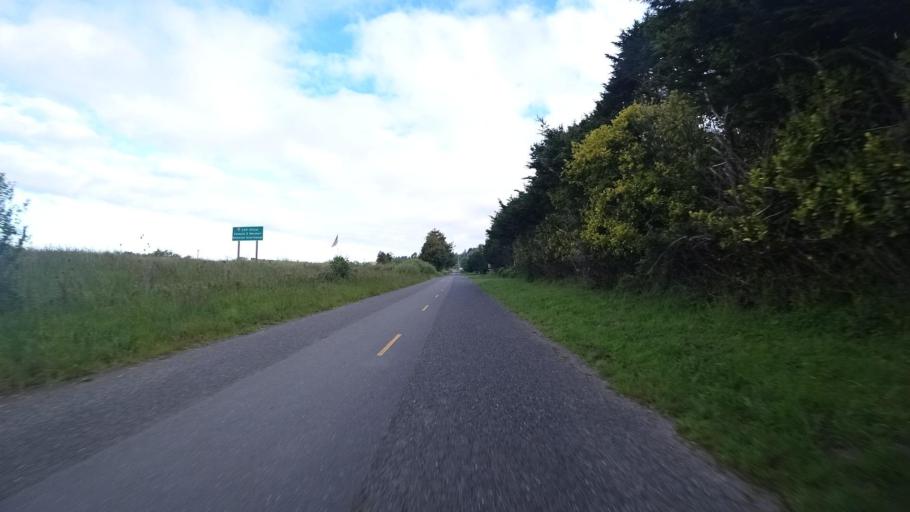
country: US
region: California
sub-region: Humboldt County
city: McKinleyville
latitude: 40.9090
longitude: -124.0887
